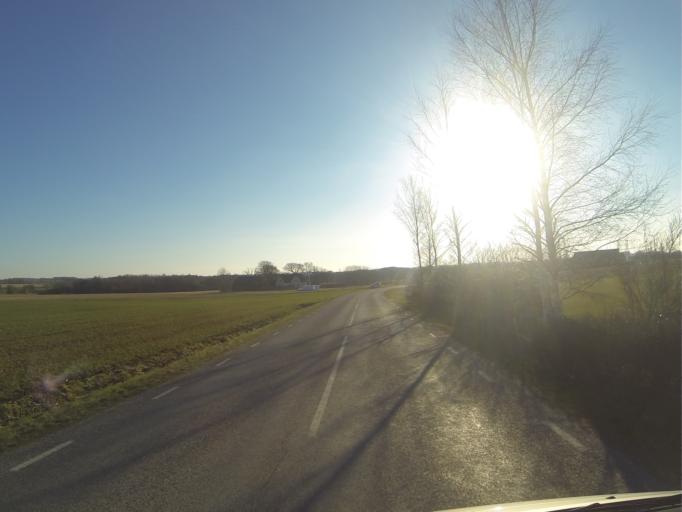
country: SE
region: Skane
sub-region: Hoors Kommun
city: Loberod
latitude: 55.8007
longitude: 13.5785
